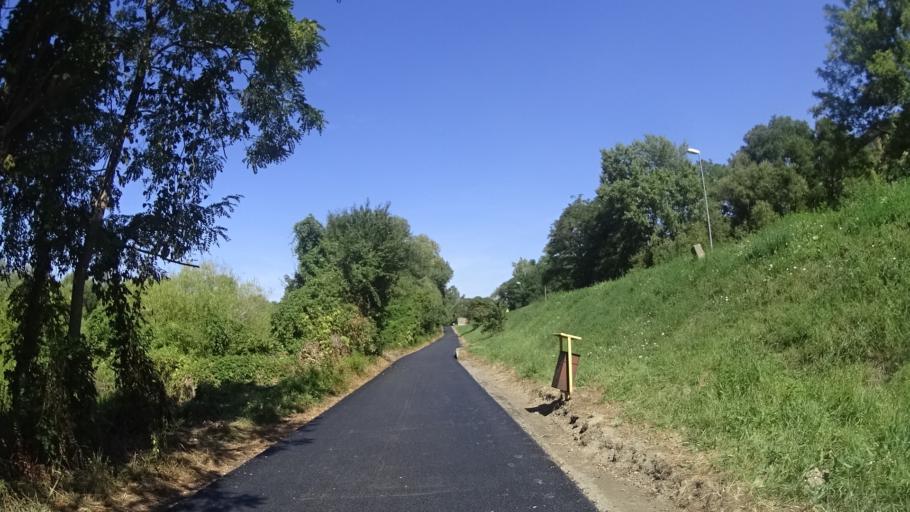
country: AT
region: Lower Austria
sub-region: Politischer Bezirk Bruck an der Leitha
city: Hainburg an der Donau
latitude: 48.1962
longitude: 16.9737
